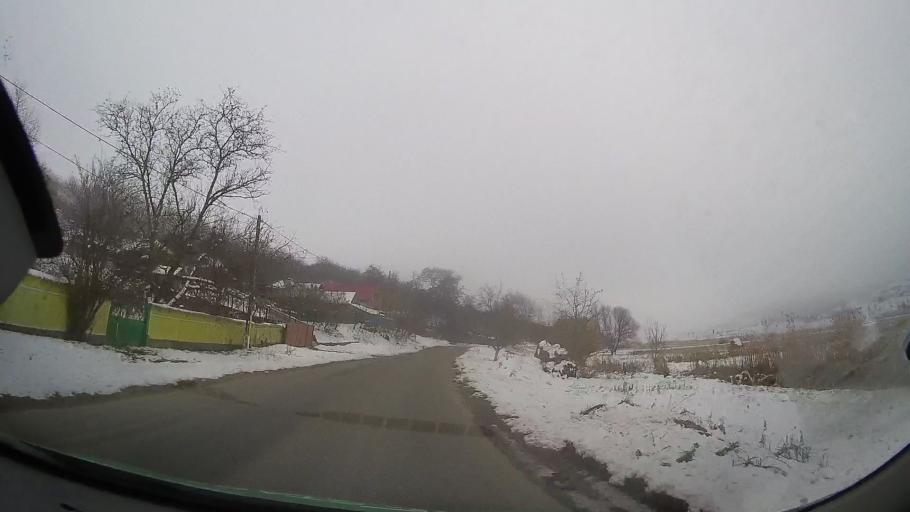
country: RO
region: Bacau
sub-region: Comuna Vultureni
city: Vultureni
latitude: 46.3592
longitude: 27.2891
